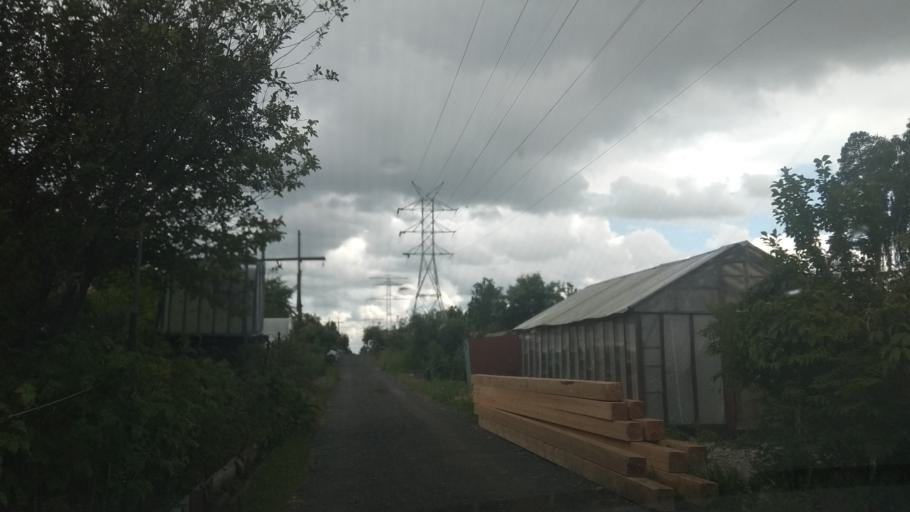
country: RU
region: Sverdlovsk
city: Verkhnyaya Pyshma
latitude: 56.9199
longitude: 60.5757
